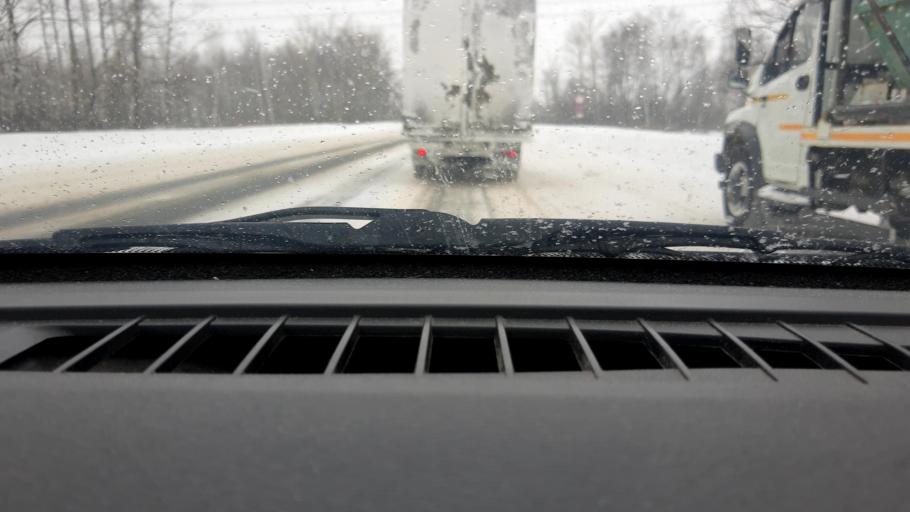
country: RU
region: Vladimir
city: Raduzhnyy
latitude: 56.0925
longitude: 40.2360
